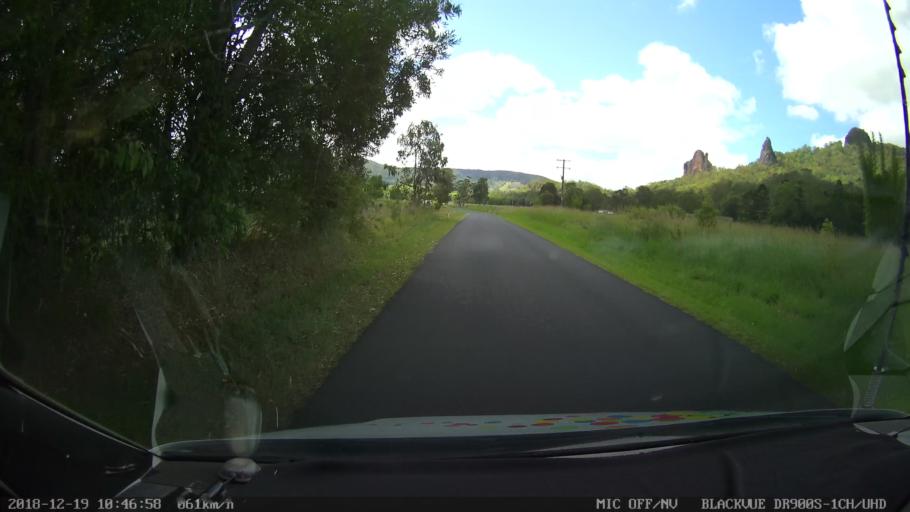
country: AU
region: New South Wales
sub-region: Lismore Municipality
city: Nimbin
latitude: -28.6039
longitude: 153.2010
